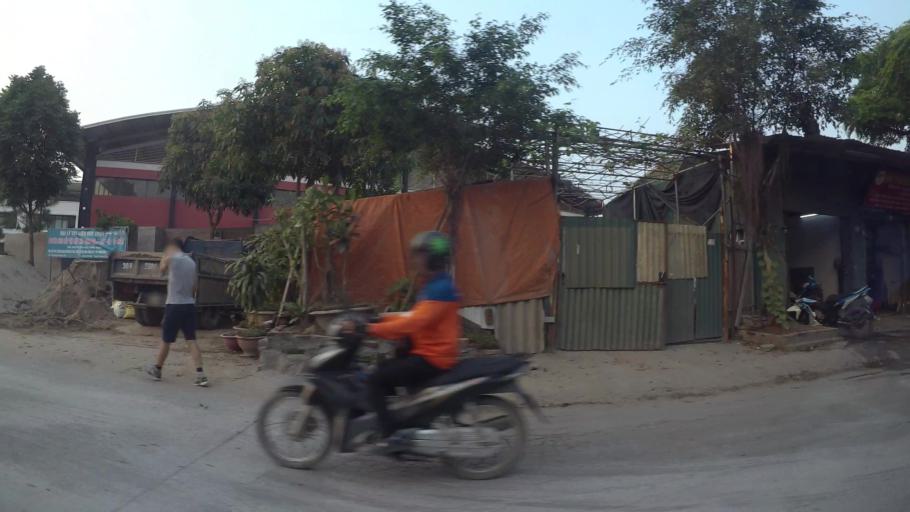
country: VN
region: Ha Noi
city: Tay Ho
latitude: 21.0726
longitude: 105.8034
